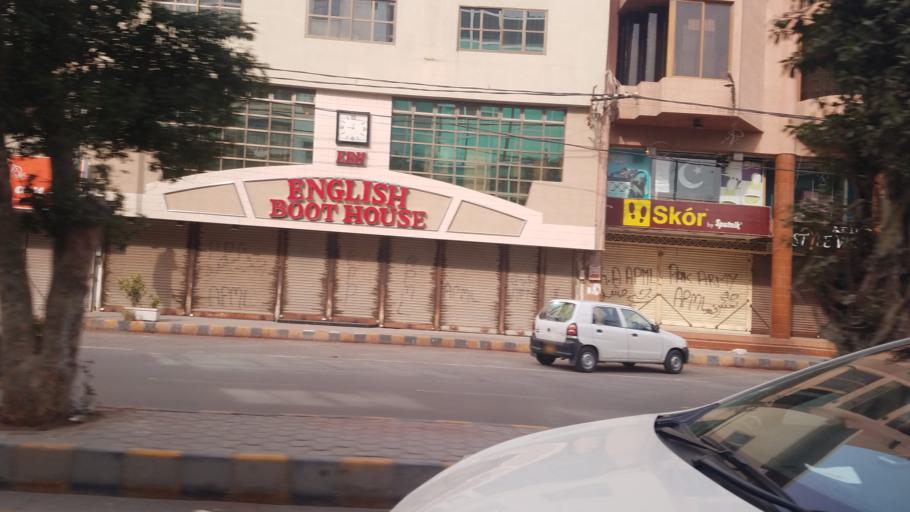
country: PK
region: Sindh
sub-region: Karachi District
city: Karachi
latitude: 24.8675
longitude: 67.0572
